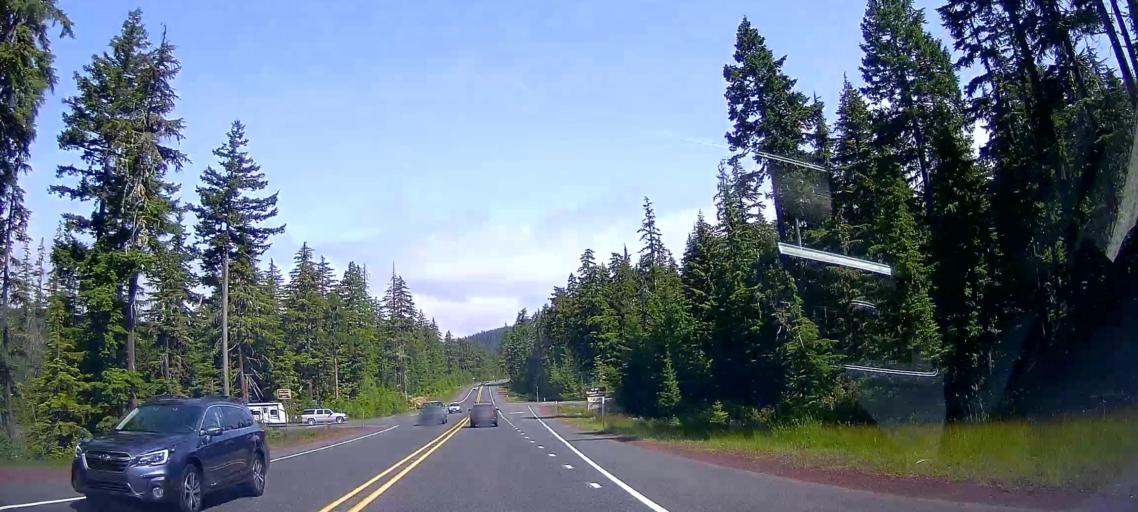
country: US
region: Oregon
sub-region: Clackamas County
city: Mount Hood Village
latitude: 45.1940
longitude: -121.6900
